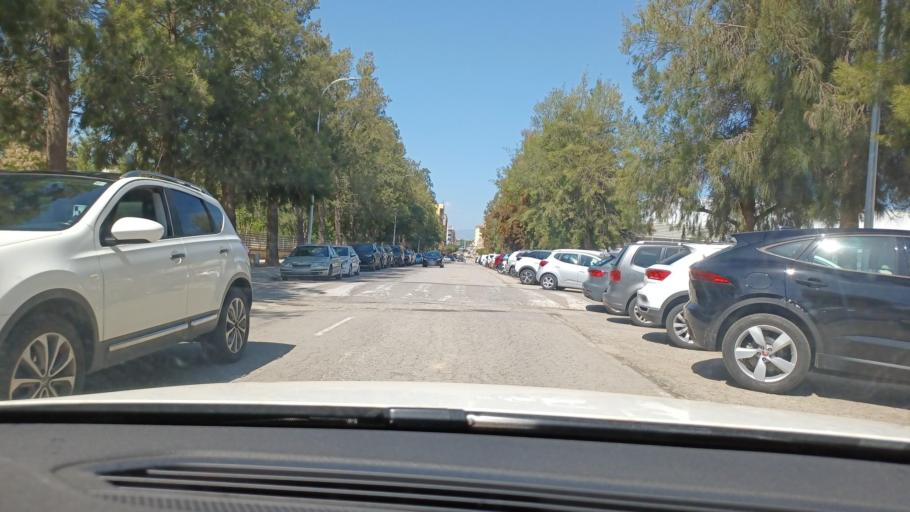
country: ES
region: Catalonia
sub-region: Provincia de Tarragona
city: Amposta
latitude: 40.7059
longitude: 0.5842
